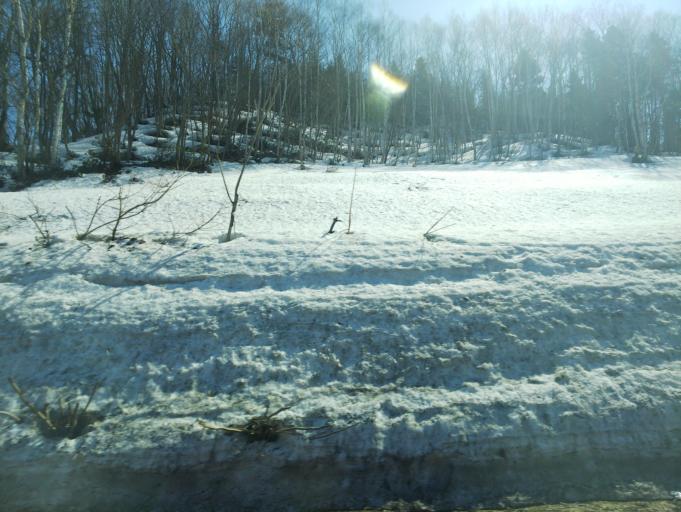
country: JP
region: Hokkaido
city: Nayoro
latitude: 44.7046
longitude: 142.2741
